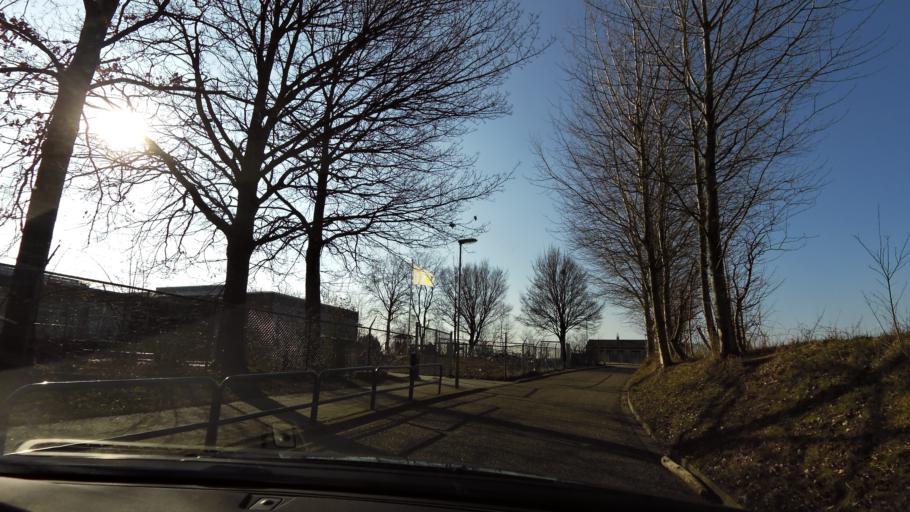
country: NL
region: Limburg
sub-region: Gemeente Simpelveld
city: Simpelveld
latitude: 50.8161
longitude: 6.0037
